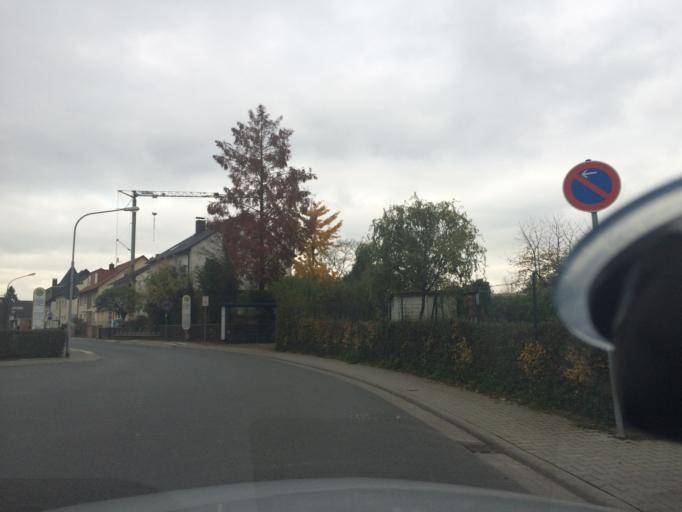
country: DE
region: Hesse
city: Pfungstadt
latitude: 49.7942
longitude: 8.6023
